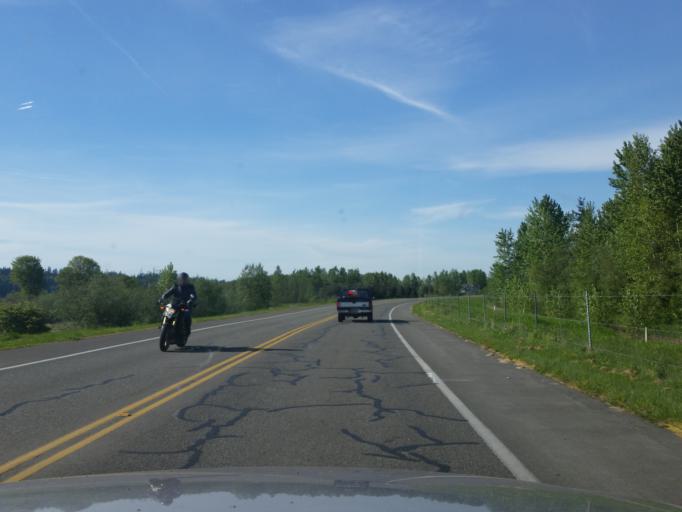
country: US
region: Washington
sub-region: Snohomish County
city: Fobes Hill
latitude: 47.9292
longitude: -122.1709
